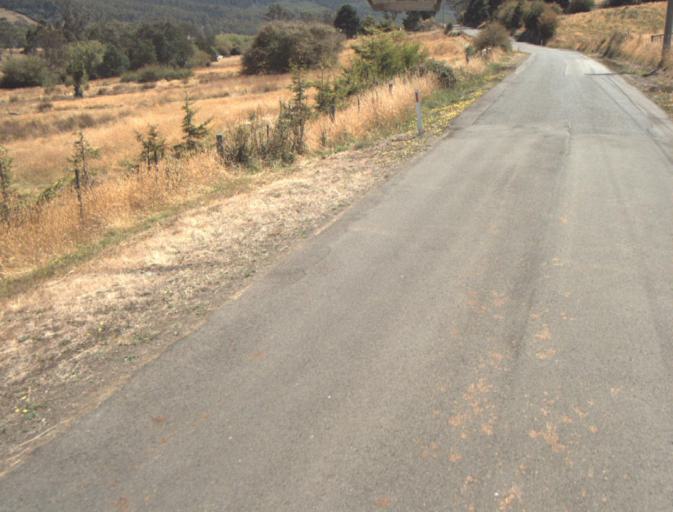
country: AU
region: Tasmania
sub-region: Launceston
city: Newstead
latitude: -41.3533
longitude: 147.3038
